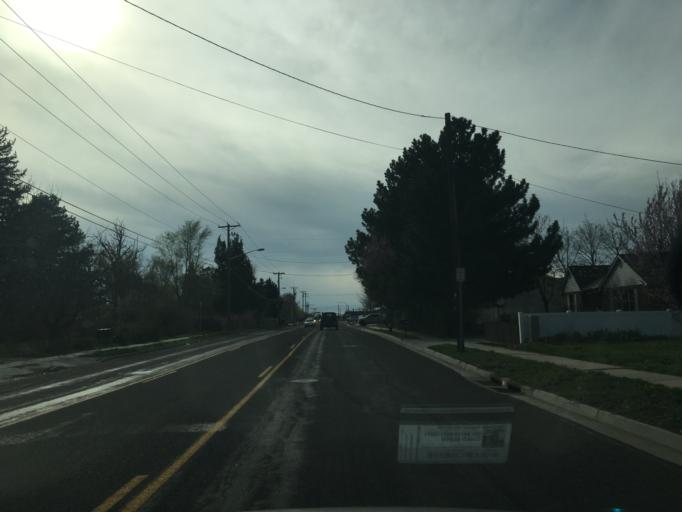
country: US
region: Utah
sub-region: Davis County
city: Layton
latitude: 41.0602
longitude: -111.9834
